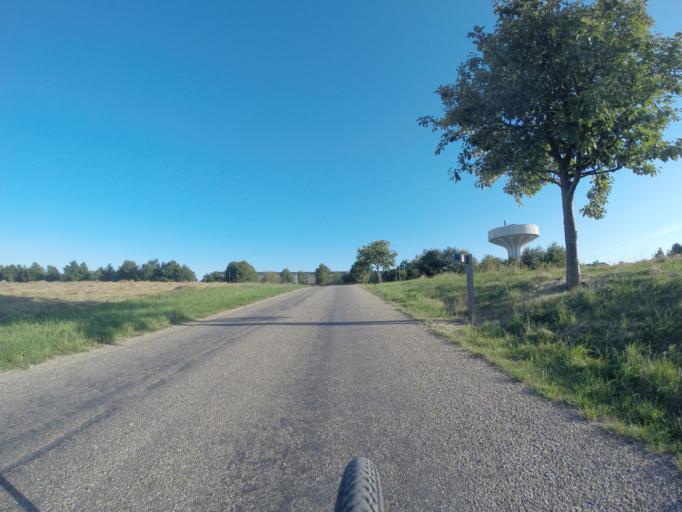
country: DK
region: Capital Region
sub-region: Herlev Kommune
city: Herlev
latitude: 55.7459
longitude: 12.4325
